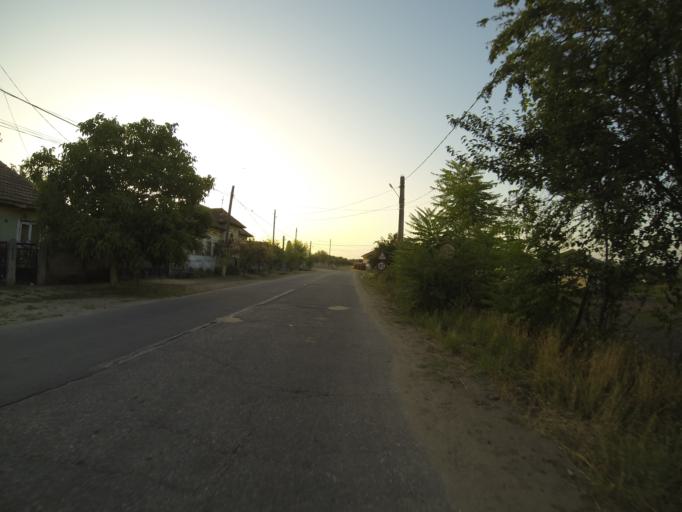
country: RO
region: Dolj
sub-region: Comuna Dobresti
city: Dobresti
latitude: 43.9809
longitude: 23.9676
